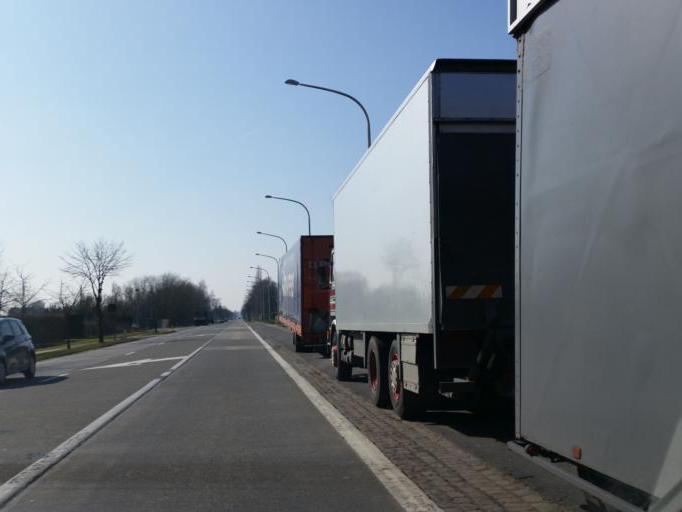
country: BE
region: Flanders
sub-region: Provincie Oost-Vlaanderen
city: Waasmunster
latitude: 51.1355
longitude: 4.0617
